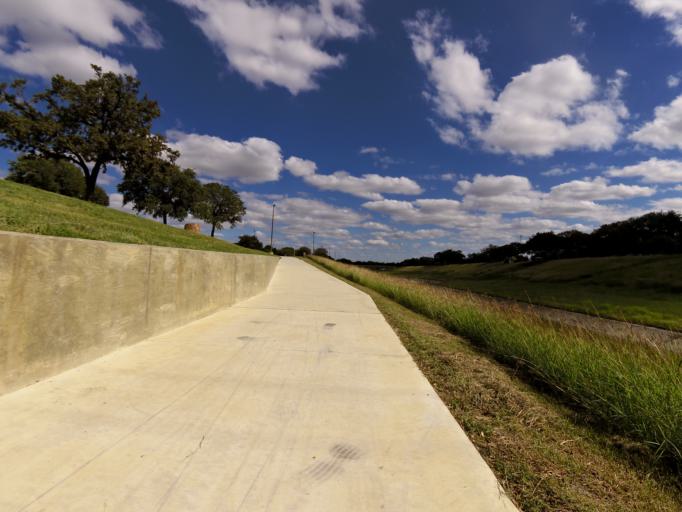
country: US
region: Texas
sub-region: Bexar County
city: San Antonio
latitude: 29.4138
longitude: -98.5242
